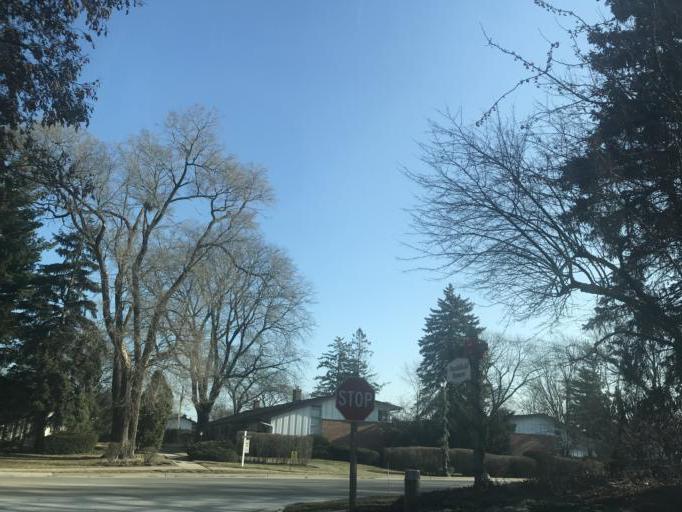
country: US
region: Illinois
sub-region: Cook County
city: Northfield
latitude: 42.0984
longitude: -87.7681
